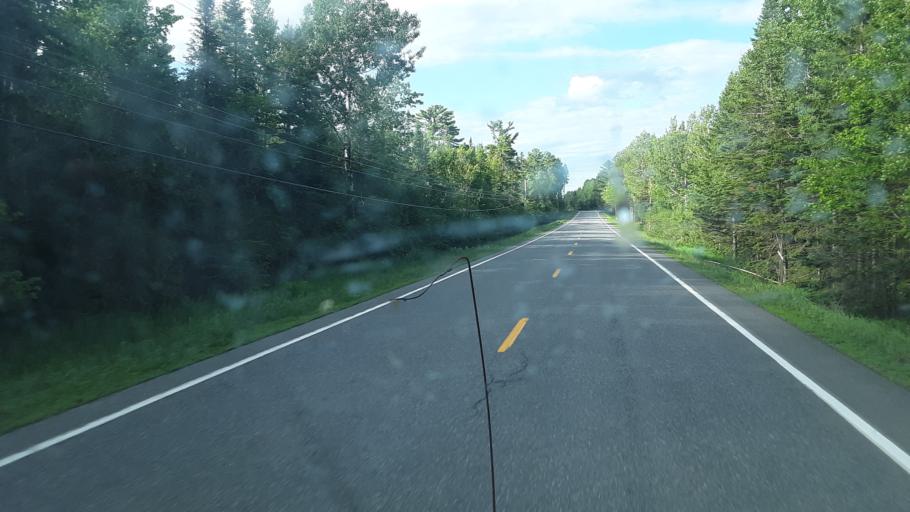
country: US
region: Maine
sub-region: Aroostook County
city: Presque Isle
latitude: 46.4801
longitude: -68.3857
